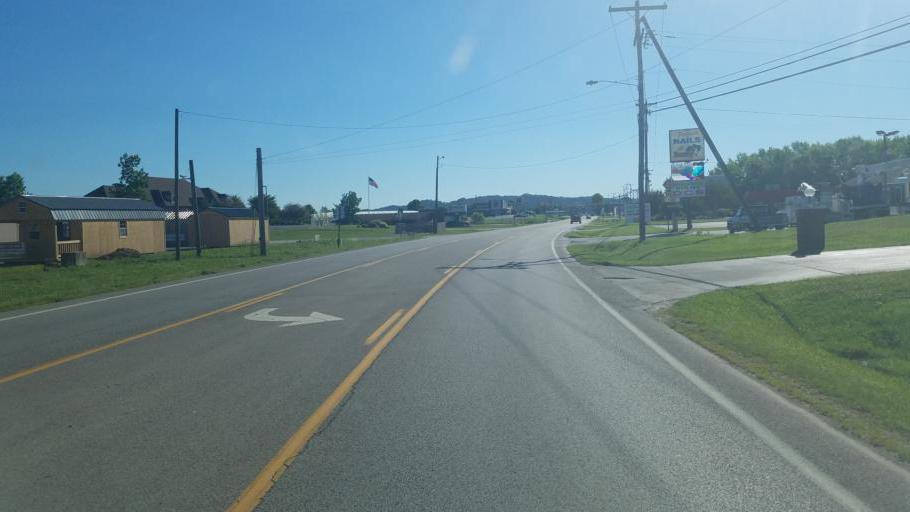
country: US
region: West Virginia
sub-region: Mason County
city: Point Pleasant
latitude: 38.8283
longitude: -82.1654
